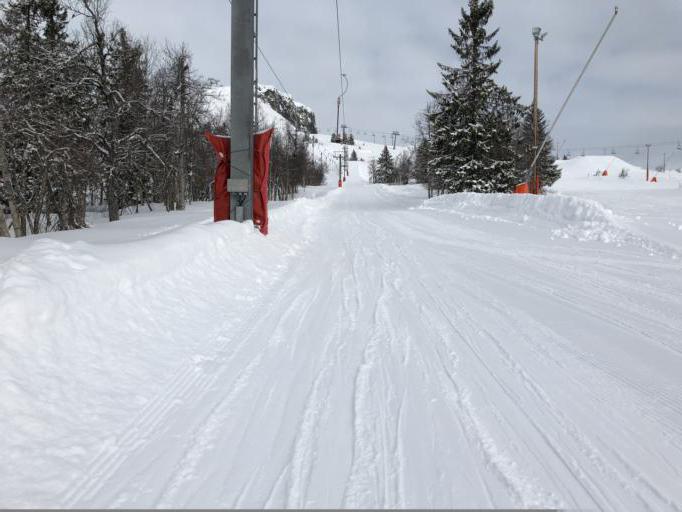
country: NO
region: Oppland
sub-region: Gausdal
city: Segalstad bru
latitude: 61.3410
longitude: 10.0871
